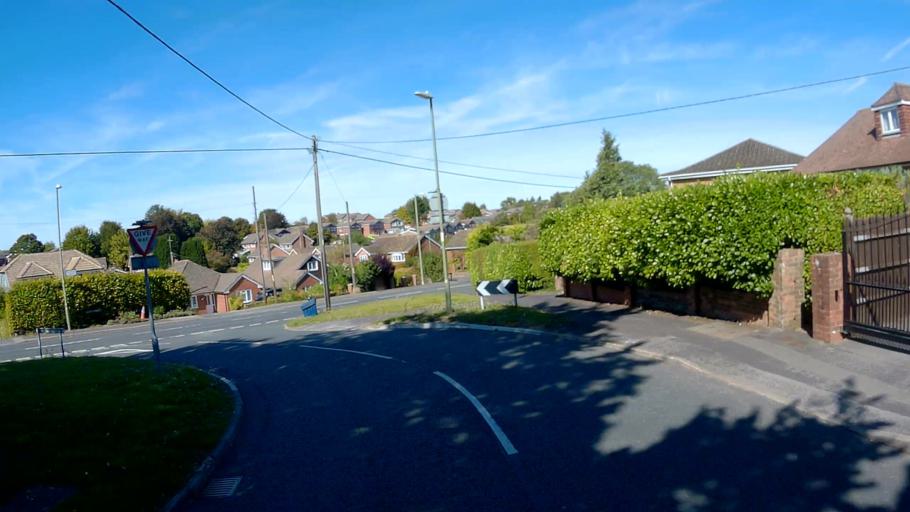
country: GB
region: England
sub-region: Hampshire
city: Basingstoke
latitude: 51.2481
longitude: -1.1389
